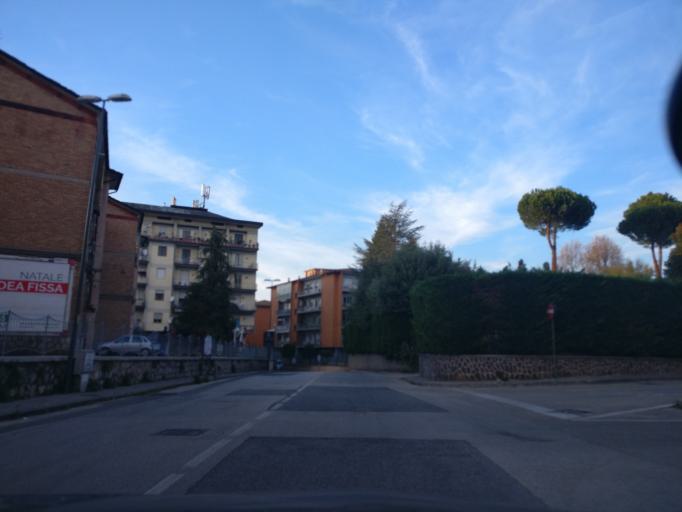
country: IT
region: Campania
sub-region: Provincia di Avellino
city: Avellino
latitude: 40.9069
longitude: 14.7981
